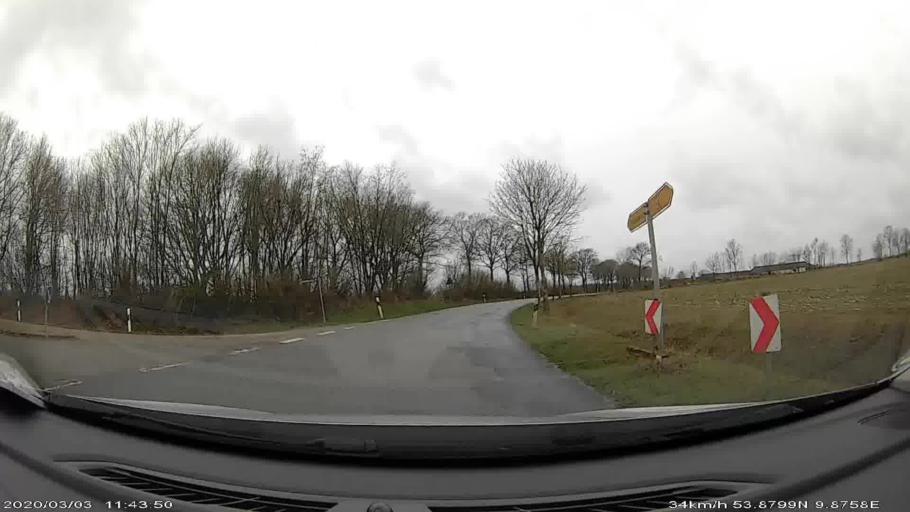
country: DE
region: Schleswig-Holstein
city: Lentfohrden
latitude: 53.8788
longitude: 9.8766
